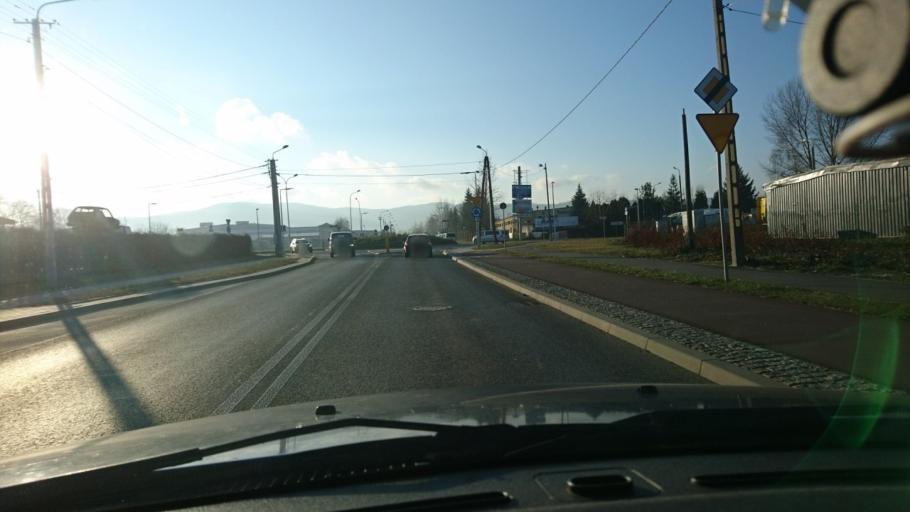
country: PL
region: Silesian Voivodeship
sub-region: Powiat bielski
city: Mazancowice
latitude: 49.8222
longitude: 18.9755
